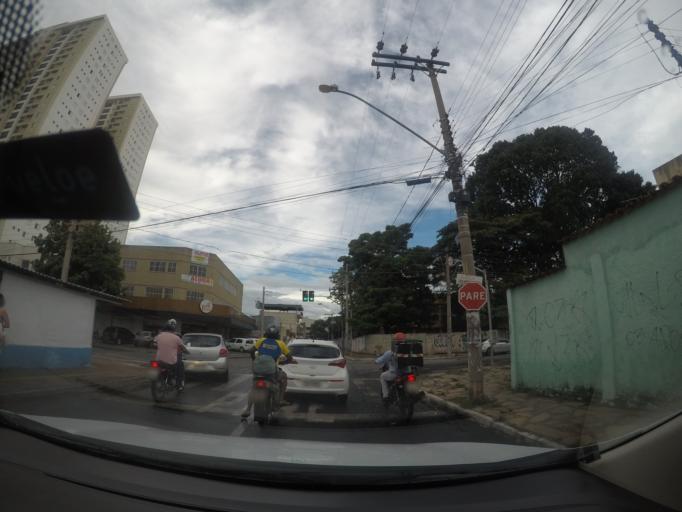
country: BR
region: Goias
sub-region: Goiania
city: Goiania
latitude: -16.6659
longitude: -49.2897
